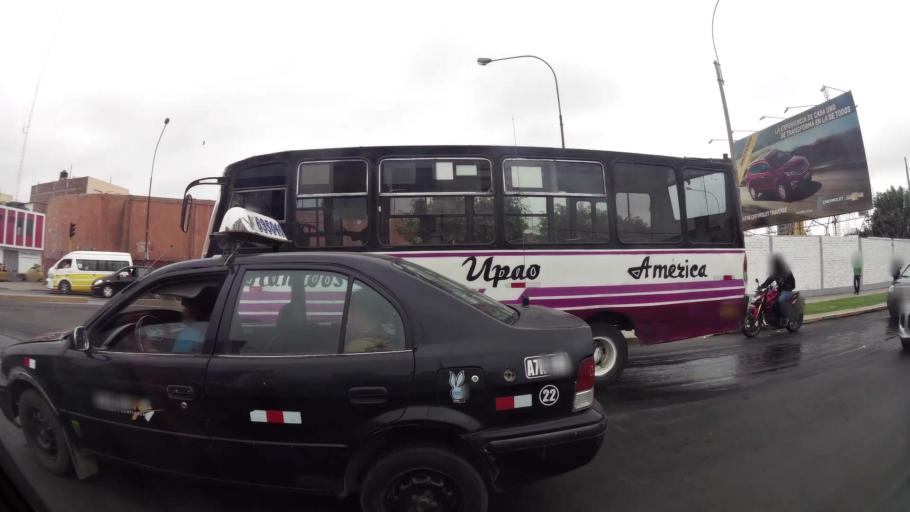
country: PE
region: La Libertad
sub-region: Provincia de Trujillo
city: Trujillo
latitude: -8.1110
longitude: -79.0330
